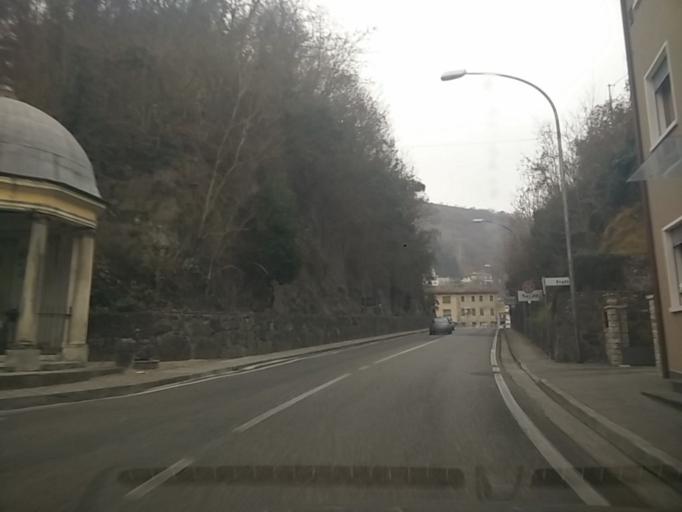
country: IT
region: Veneto
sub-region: Provincia di Treviso
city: Tarzo
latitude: 45.9798
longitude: 12.2296
